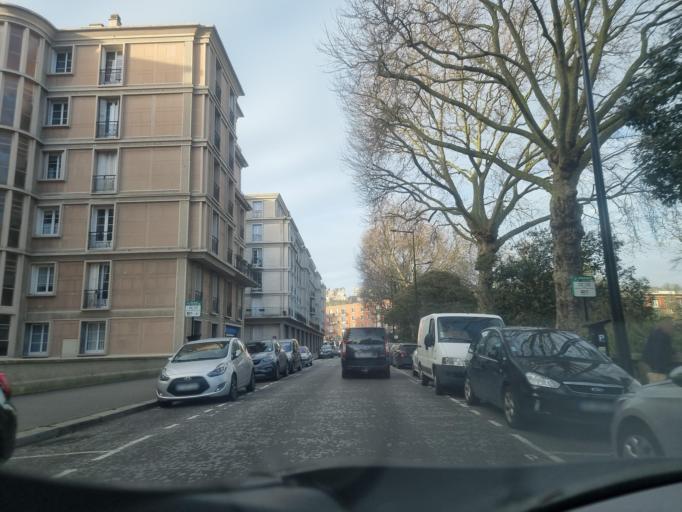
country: FR
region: Haute-Normandie
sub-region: Departement de la Seine-Maritime
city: Le Havre
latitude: 49.4939
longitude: 0.1010
